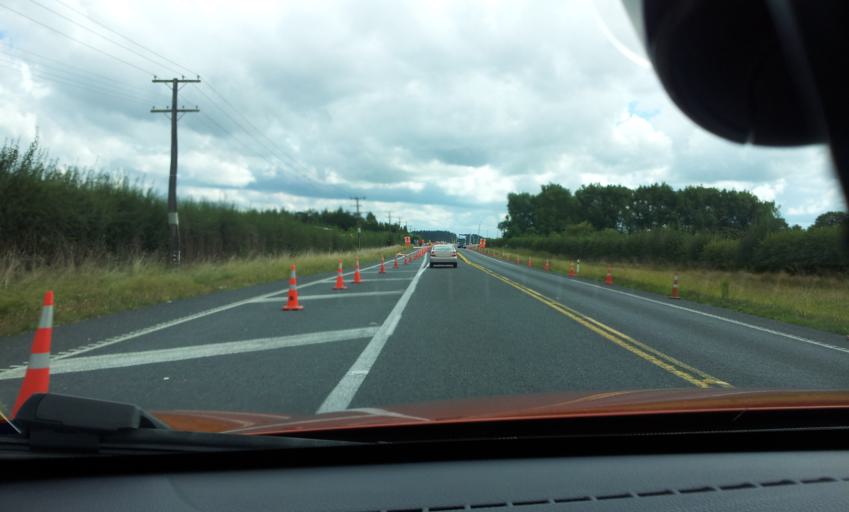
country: NZ
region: Waikato
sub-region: Waipa District
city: Cambridge
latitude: -37.9004
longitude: 175.5140
